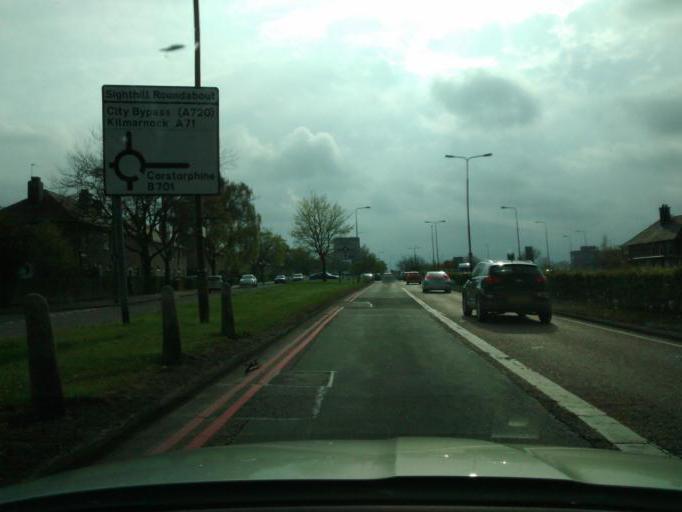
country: GB
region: Scotland
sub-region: Edinburgh
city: Colinton
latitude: 55.9242
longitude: -3.2786
